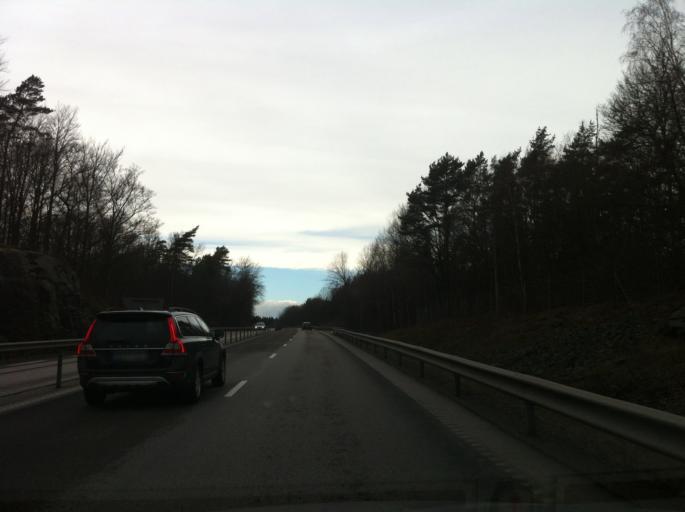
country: SE
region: Blekinge
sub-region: Ronneby Kommun
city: Brakne-Hoby
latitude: 56.2126
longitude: 15.0885
